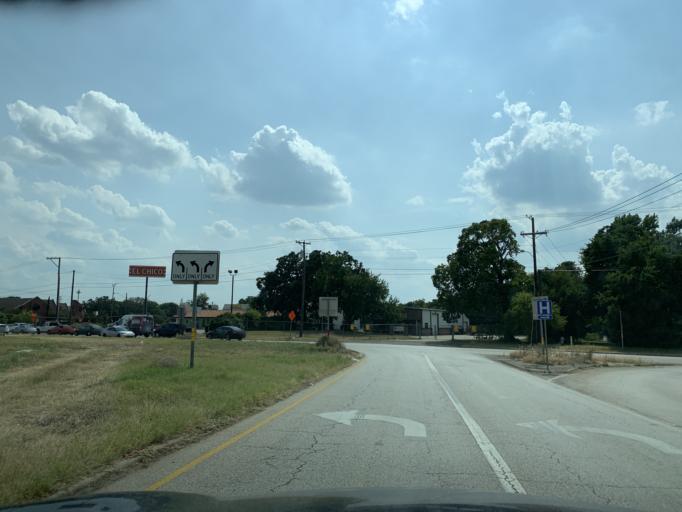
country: US
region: Texas
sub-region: Tarrant County
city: Richland Hills
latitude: 32.8103
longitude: -97.2119
